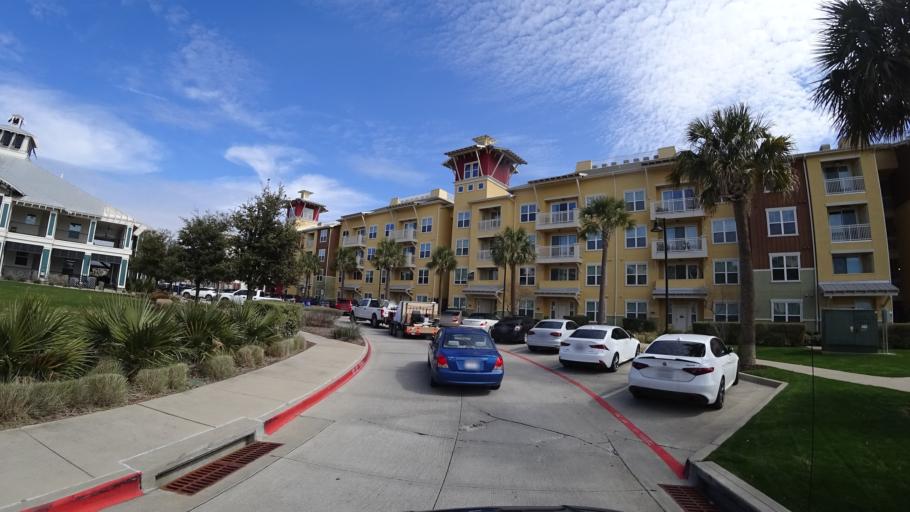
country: US
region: Texas
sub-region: Denton County
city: Lewisville
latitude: 33.0054
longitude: -96.9602
